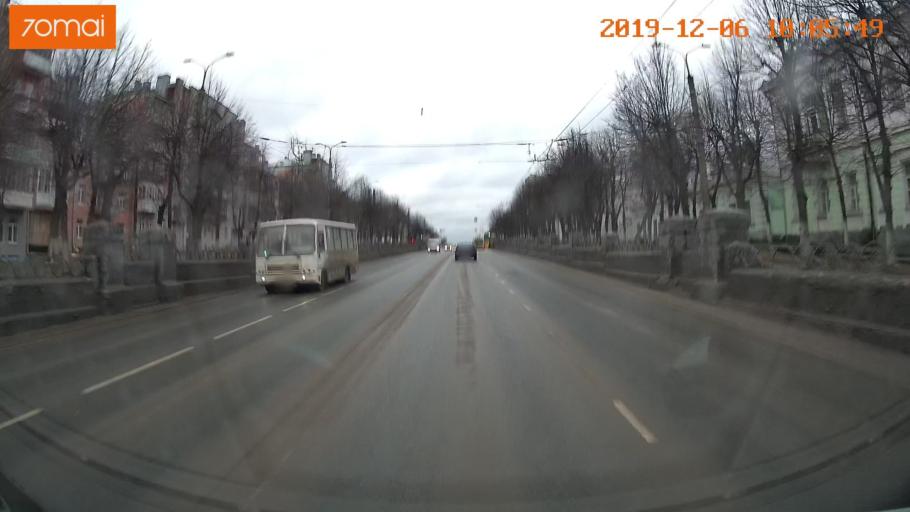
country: RU
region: Ivanovo
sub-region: Gorod Ivanovo
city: Ivanovo
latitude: 57.0048
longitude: 40.9734
